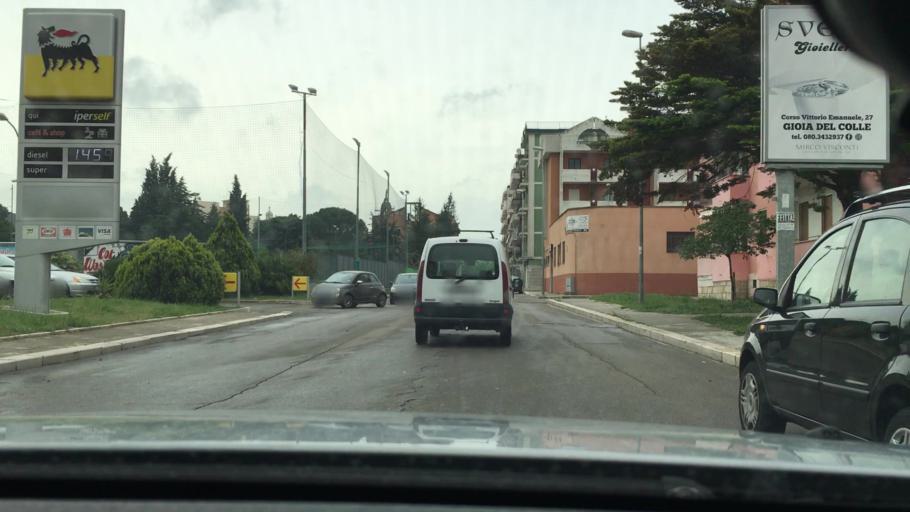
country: IT
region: Apulia
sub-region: Provincia di Bari
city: Gioia del Colle
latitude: 40.8060
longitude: 16.9241
